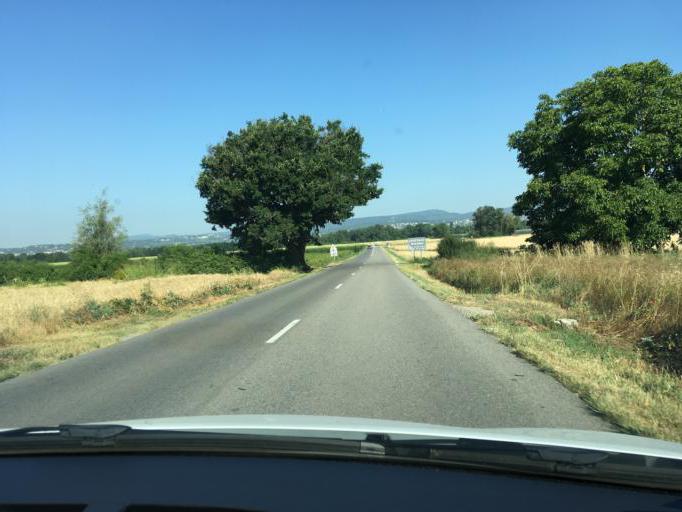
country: FR
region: Provence-Alpes-Cote d'Azur
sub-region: Departement des Alpes-de-Haute-Provence
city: Manosque
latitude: 43.7942
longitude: 5.8345
